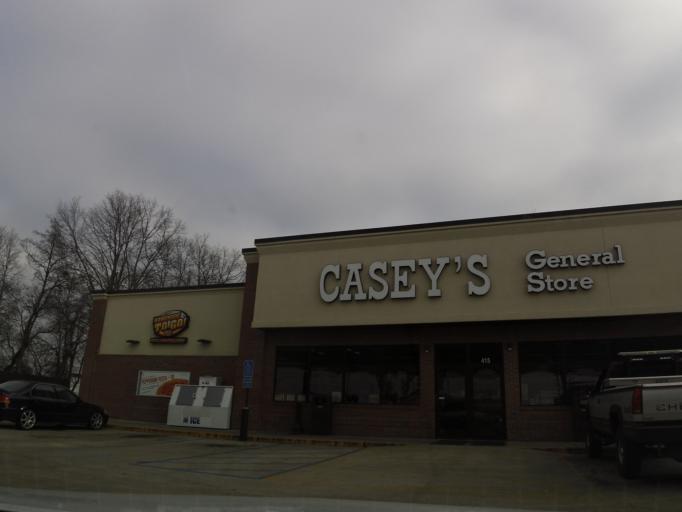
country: US
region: Indiana
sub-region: Bartholomew County
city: Columbus
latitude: 39.1938
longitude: -85.8940
